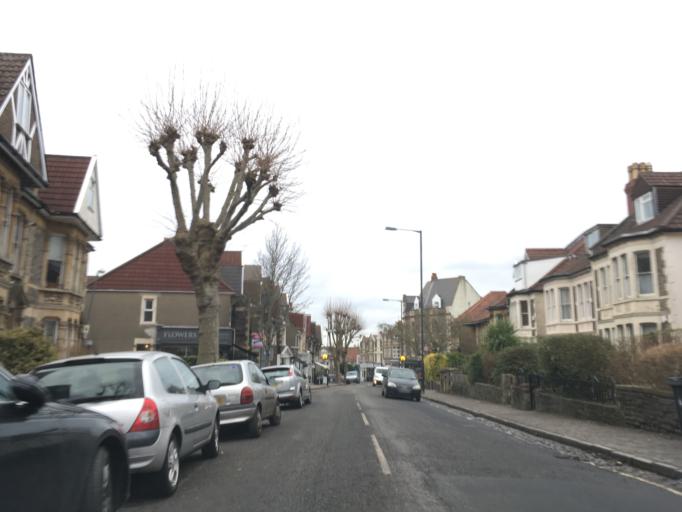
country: GB
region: England
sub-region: Bristol
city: Bristol
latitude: 51.4772
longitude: -2.6090
